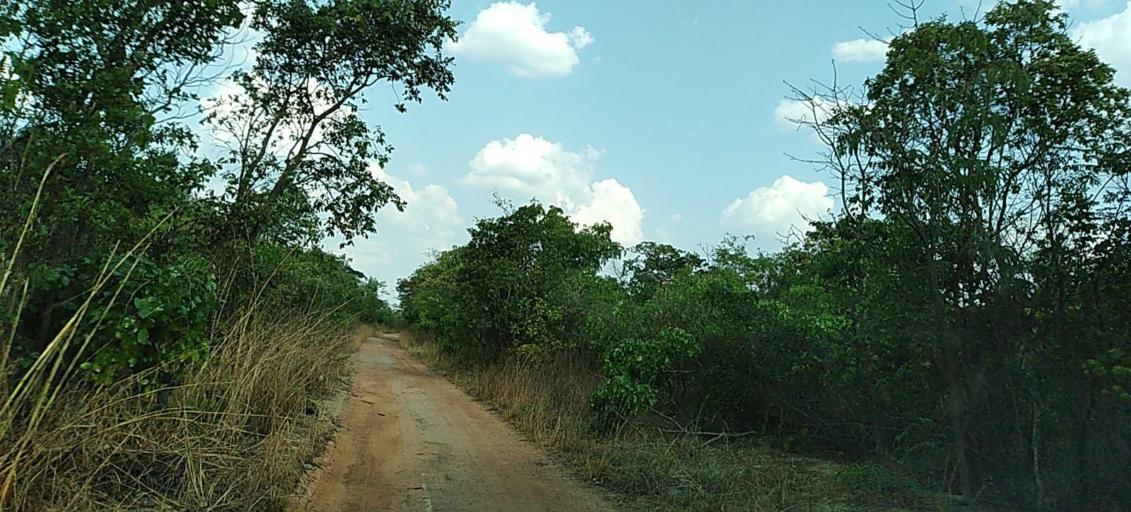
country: ZM
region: Copperbelt
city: Luanshya
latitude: -13.1548
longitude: 28.3219
